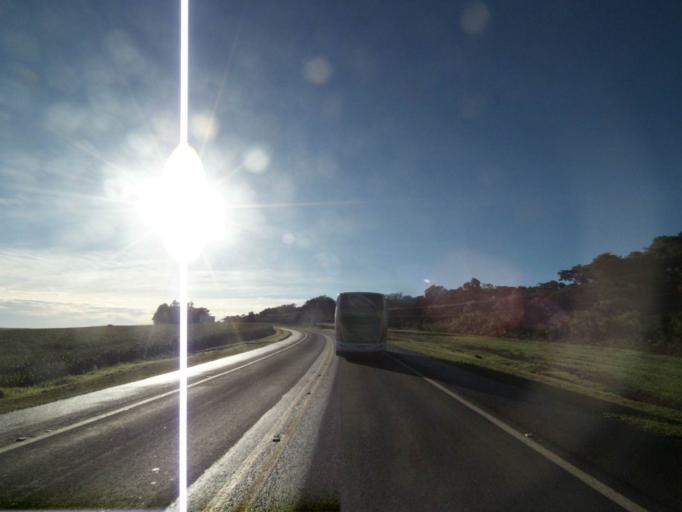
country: BR
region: Parana
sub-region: Matelandia
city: Matelandia
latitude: -25.1127
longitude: -53.7701
